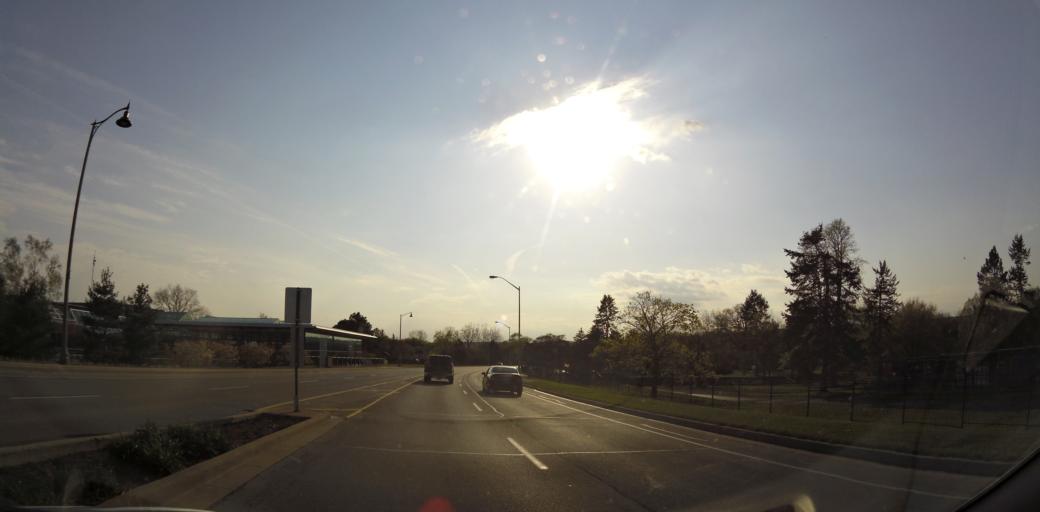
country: CA
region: Ontario
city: Hamilton
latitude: 43.2909
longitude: -79.8747
